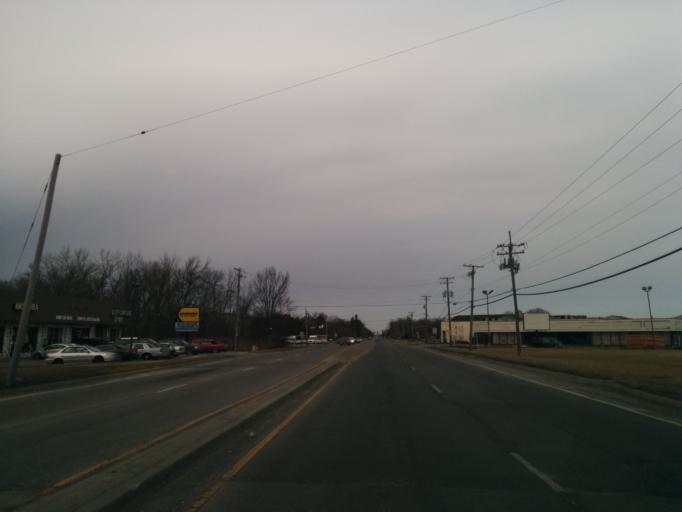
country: US
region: Illinois
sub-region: Cook County
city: Des Plaines
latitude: 42.0905
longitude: -87.8736
